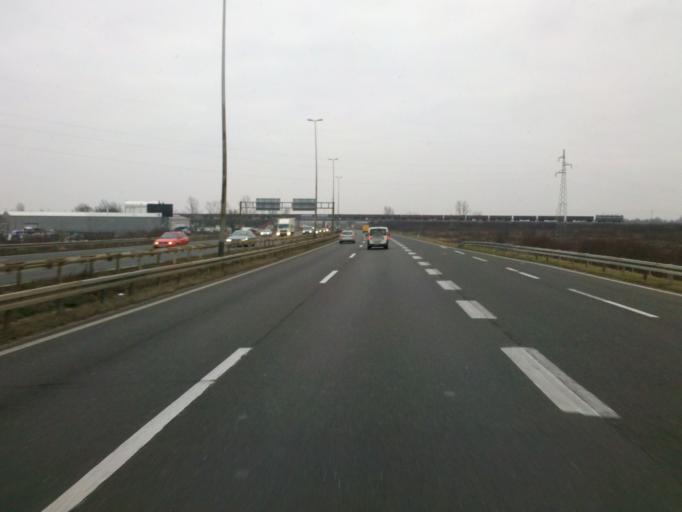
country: HR
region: Grad Zagreb
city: Zadvorsko
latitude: 45.7542
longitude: 15.9052
